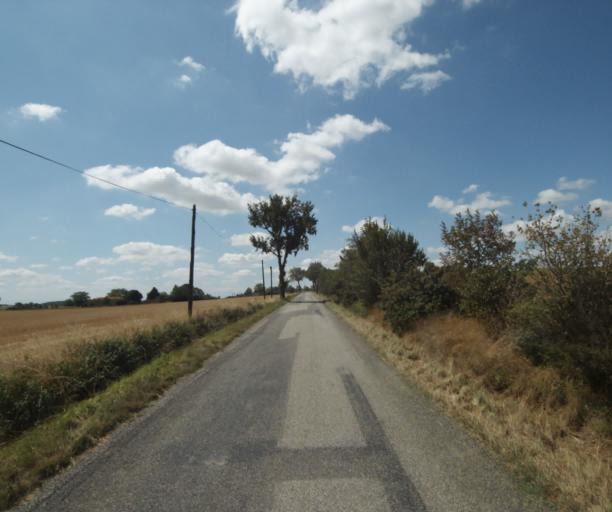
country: FR
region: Midi-Pyrenees
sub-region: Departement de la Haute-Garonne
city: Saint-Felix-Lauragais
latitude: 43.4645
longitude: 1.8417
